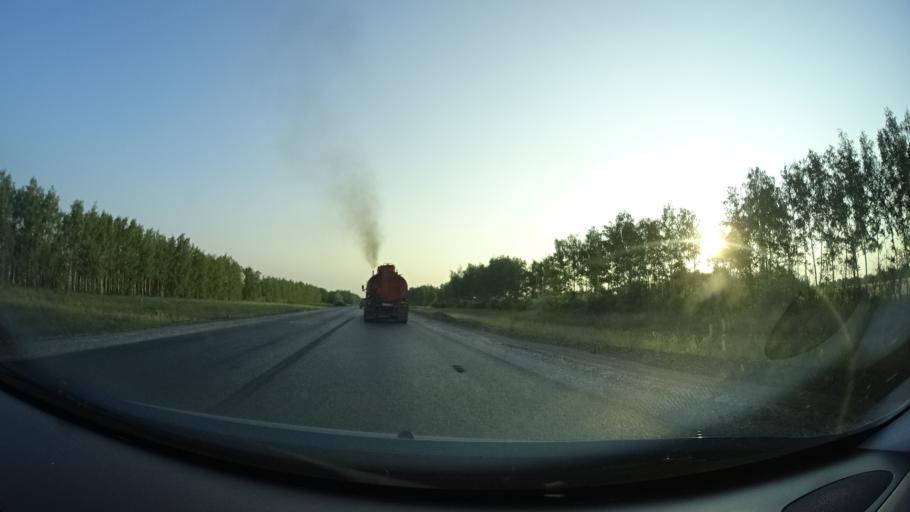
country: RU
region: Samara
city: Isakly
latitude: 53.9922
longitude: 51.5272
